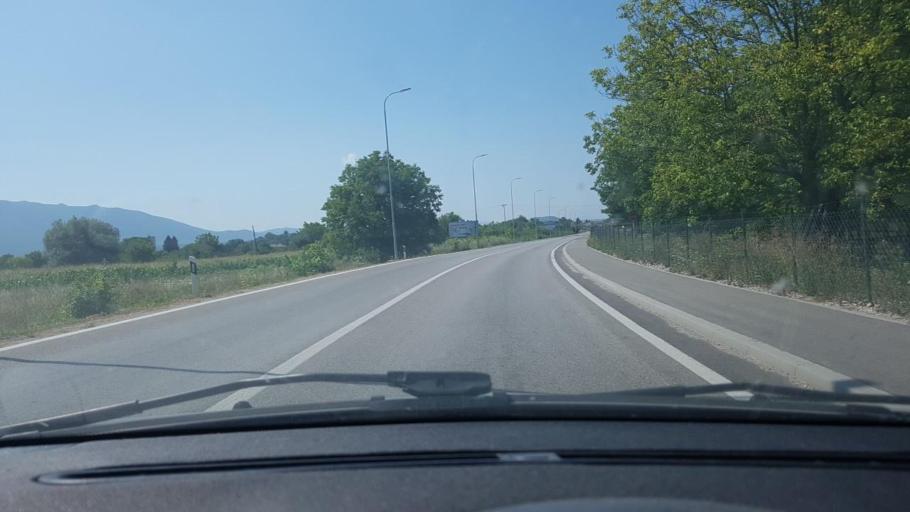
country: BA
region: Federation of Bosnia and Herzegovina
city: Bihac
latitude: 44.8079
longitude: 15.8857
